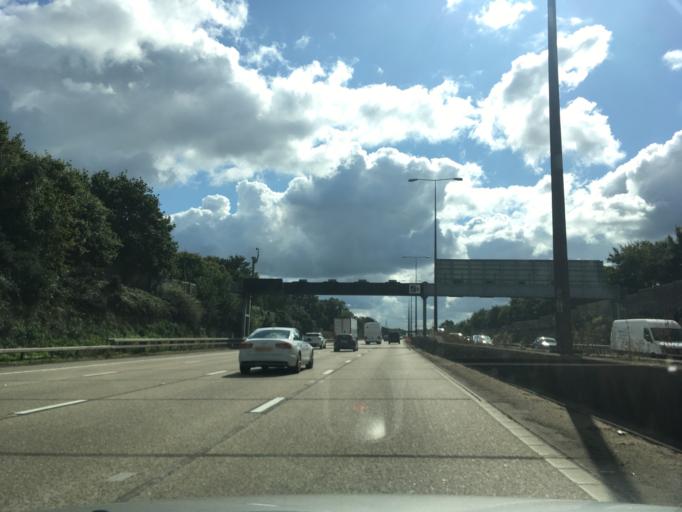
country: GB
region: England
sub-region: Surrey
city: Addlestone
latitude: 51.3622
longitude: -0.4991
